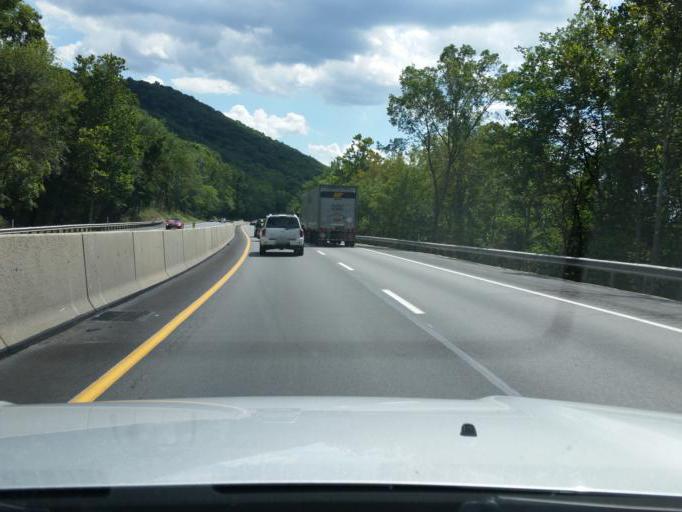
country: US
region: Pennsylvania
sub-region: Bedford County
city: Everett
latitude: 40.0099
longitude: -78.4101
